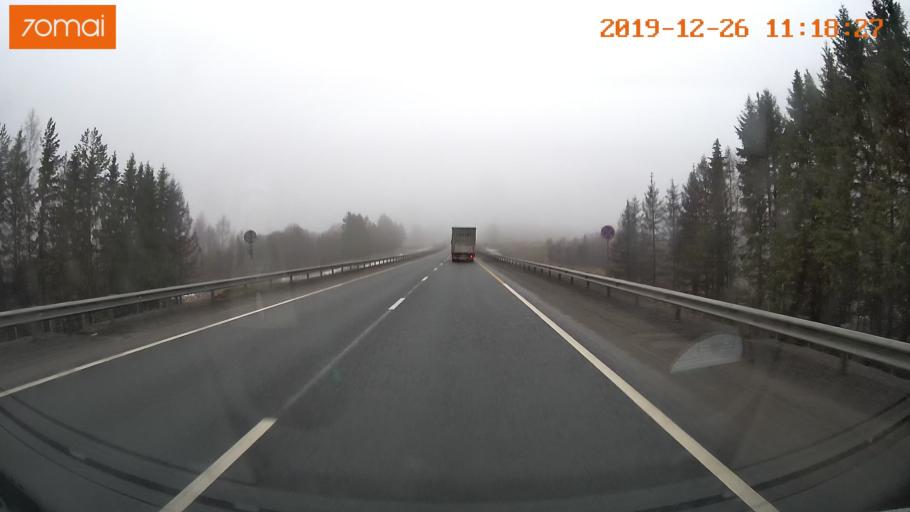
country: RU
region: Vologda
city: Chebsara
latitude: 59.1192
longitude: 39.0339
